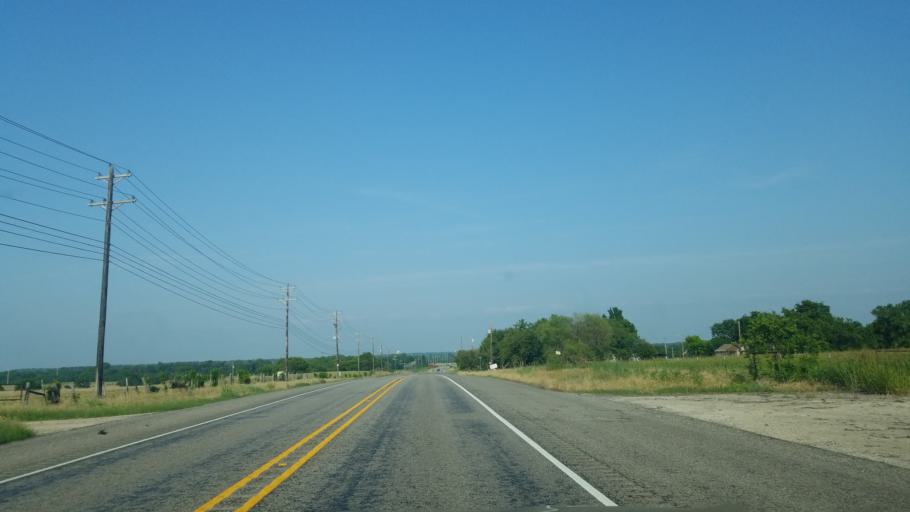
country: US
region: Texas
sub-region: Denton County
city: Aubrey
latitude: 33.3071
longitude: -97.0528
